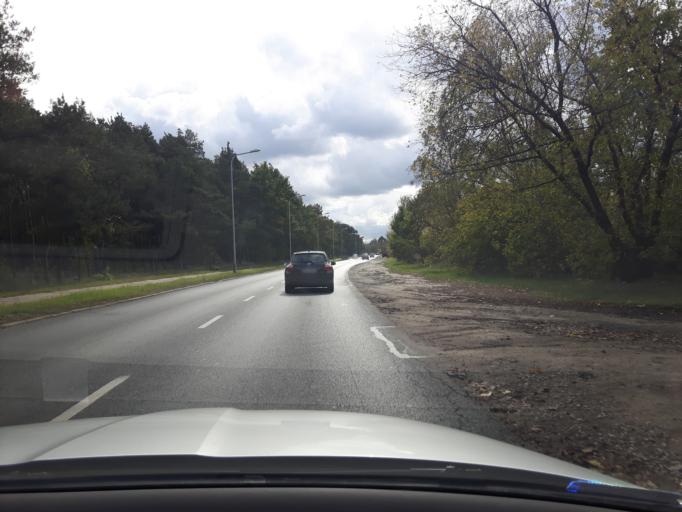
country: PL
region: Masovian Voivodeship
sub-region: Warszawa
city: Rembertow
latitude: 52.2343
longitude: 21.1436
